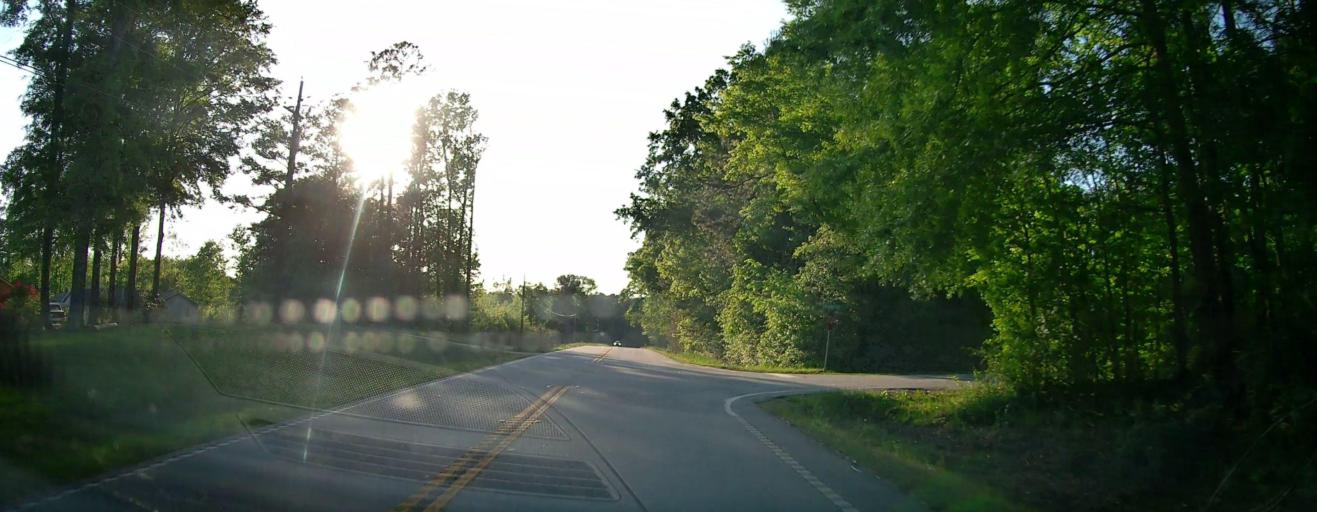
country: US
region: Georgia
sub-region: Walton County
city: Social Circle
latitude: 33.5665
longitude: -83.7588
